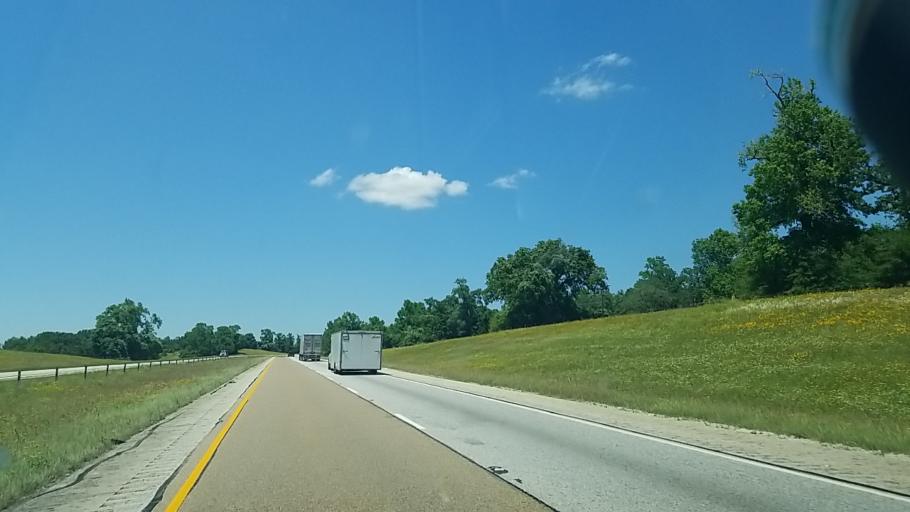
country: US
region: Texas
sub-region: Leon County
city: Centerville
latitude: 31.2060
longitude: -95.9958
